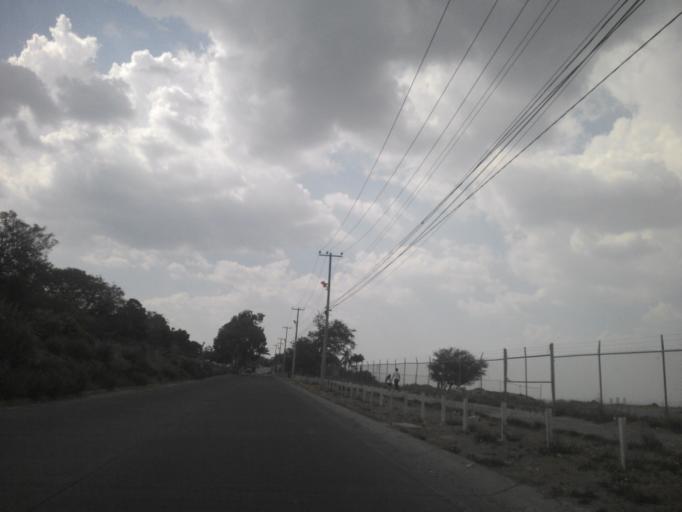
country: MX
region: Jalisco
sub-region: Tlajomulco de Zuniga
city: La Tijera
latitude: 20.6153
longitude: -103.4012
